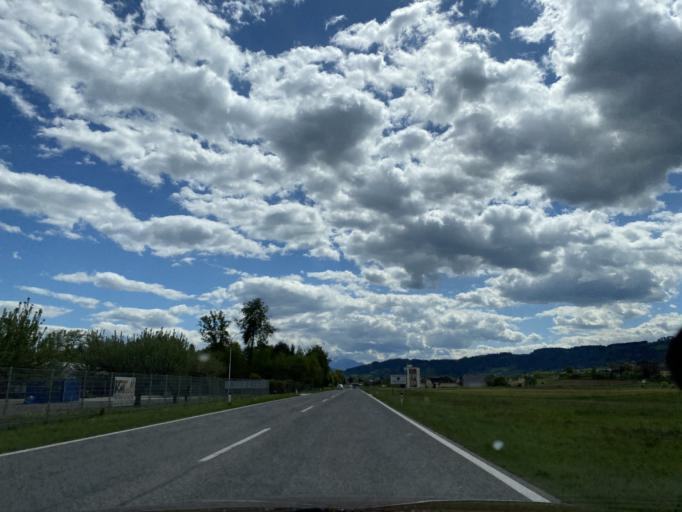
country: AT
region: Carinthia
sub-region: Politischer Bezirk Wolfsberg
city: Sankt Andrae
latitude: 46.8023
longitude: 14.8290
